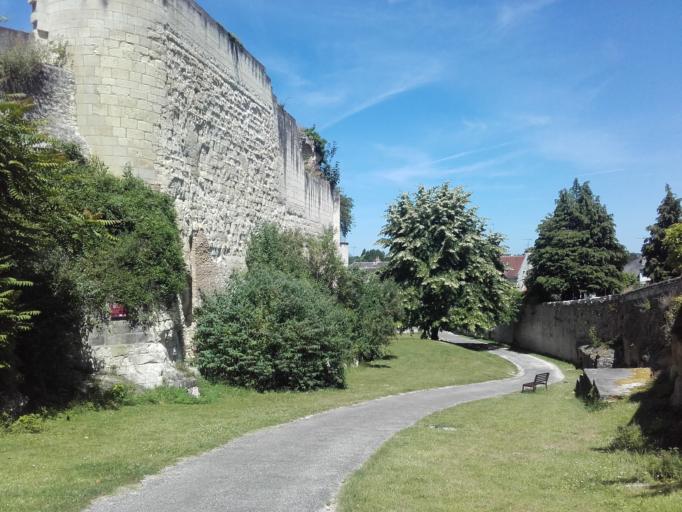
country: FR
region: Centre
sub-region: Departement d'Indre-et-Loire
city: Loches
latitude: 47.1257
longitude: 0.9986
